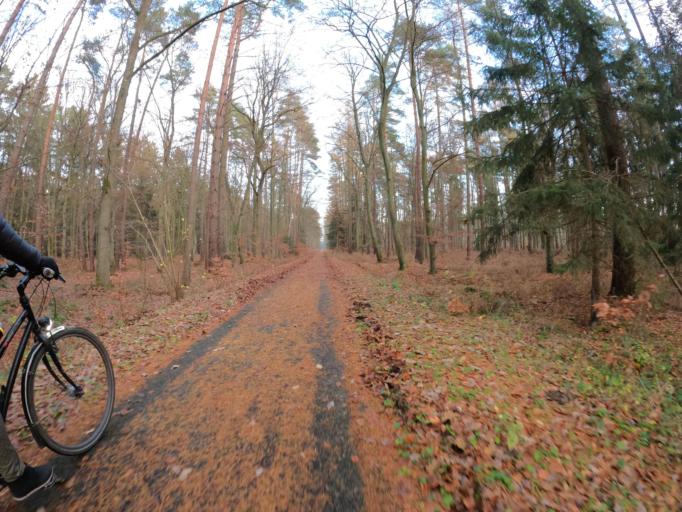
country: PL
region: West Pomeranian Voivodeship
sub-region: Powiat policki
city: Nowe Warpno
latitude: 53.6911
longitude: 14.2931
